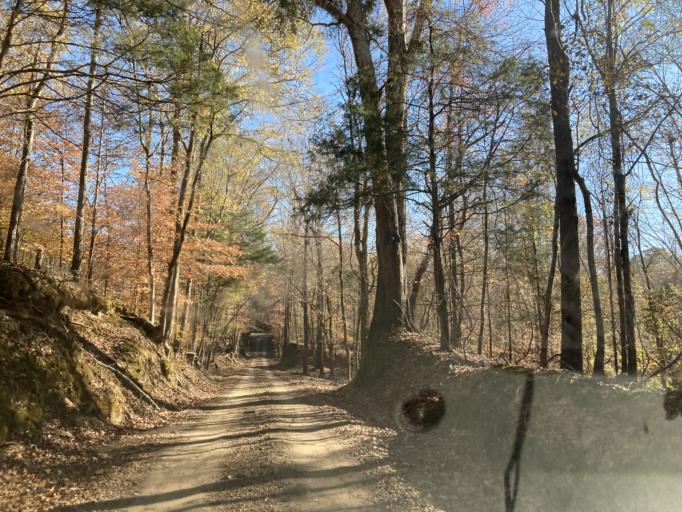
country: US
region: Mississippi
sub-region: Madison County
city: Kearney Park
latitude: 32.6185
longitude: -90.4588
